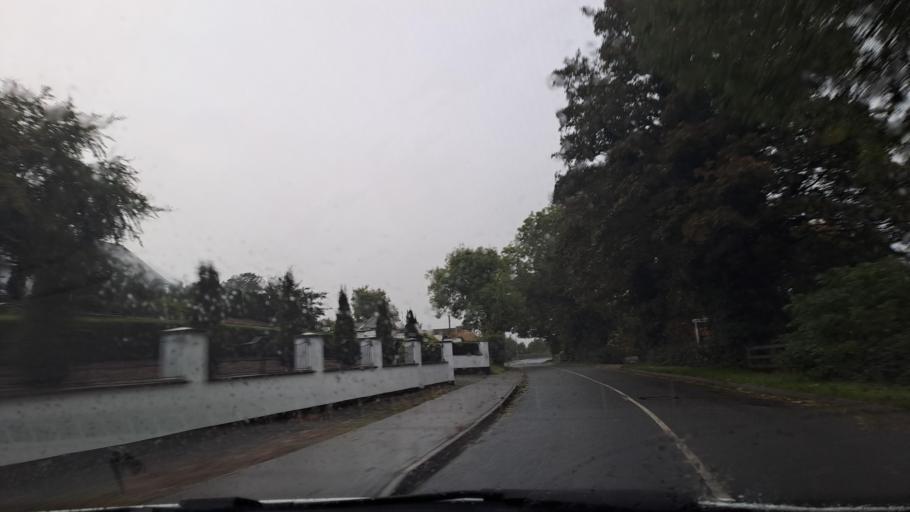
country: IE
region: Ulster
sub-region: County Monaghan
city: Carrickmacross
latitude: 53.9773
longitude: -6.7072
